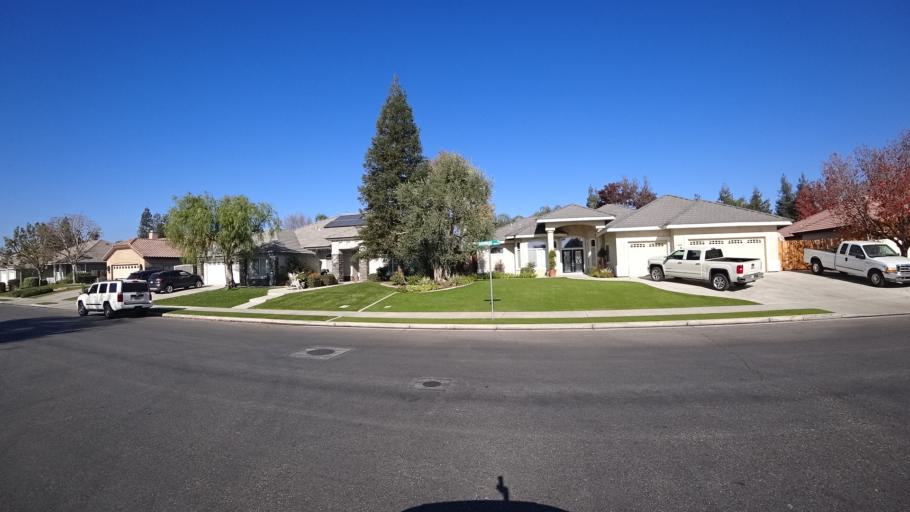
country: US
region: California
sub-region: Kern County
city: Rosedale
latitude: 35.3660
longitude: -119.1425
